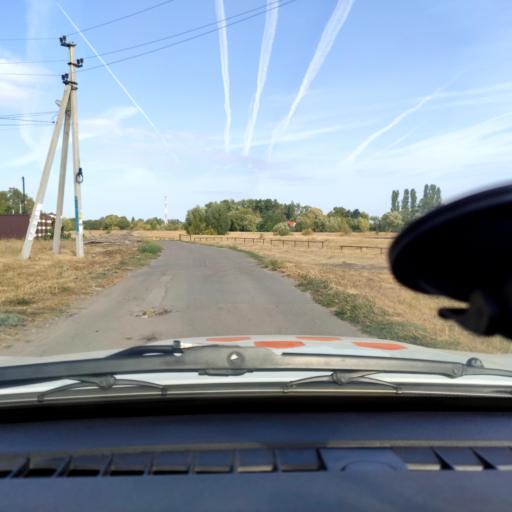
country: RU
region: Voronezj
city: Novaya Usman'
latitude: 51.6287
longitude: 39.4113
